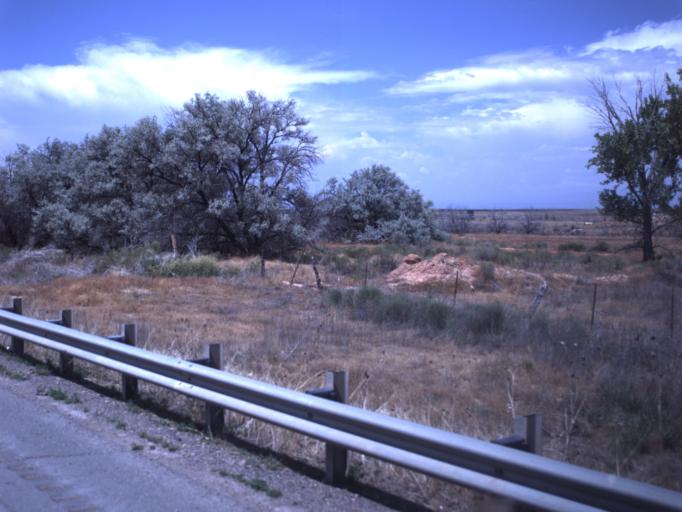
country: US
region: Utah
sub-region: Duchesne County
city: Roosevelt
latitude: 40.3048
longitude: -109.7733
